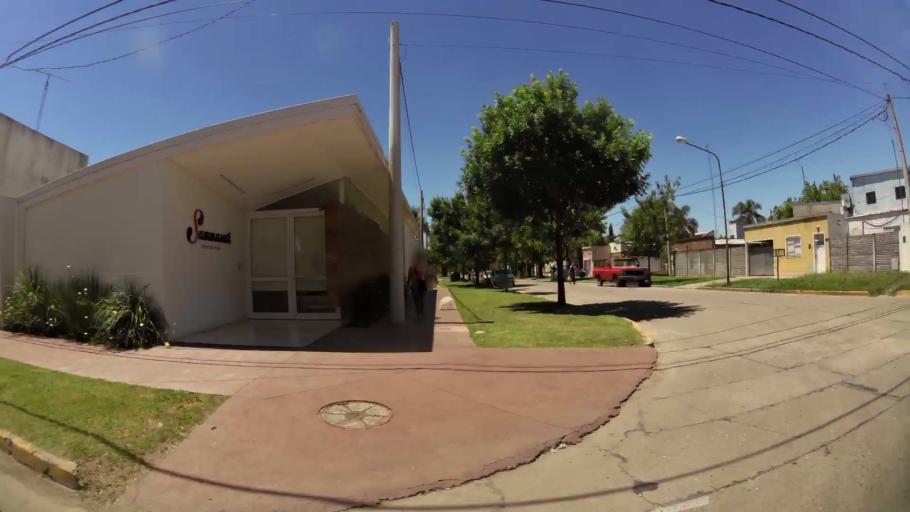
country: AR
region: Santa Fe
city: Rafaela
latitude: -31.2535
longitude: -61.4637
